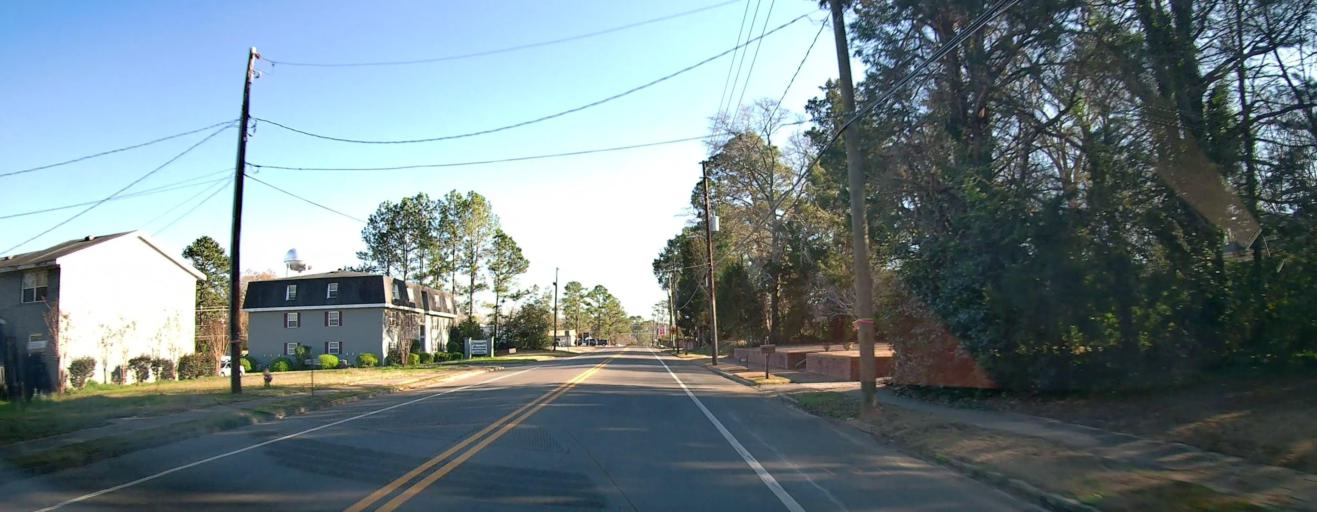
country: US
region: Georgia
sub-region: Sumter County
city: Americus
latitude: 32.0542
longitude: -84.2266
